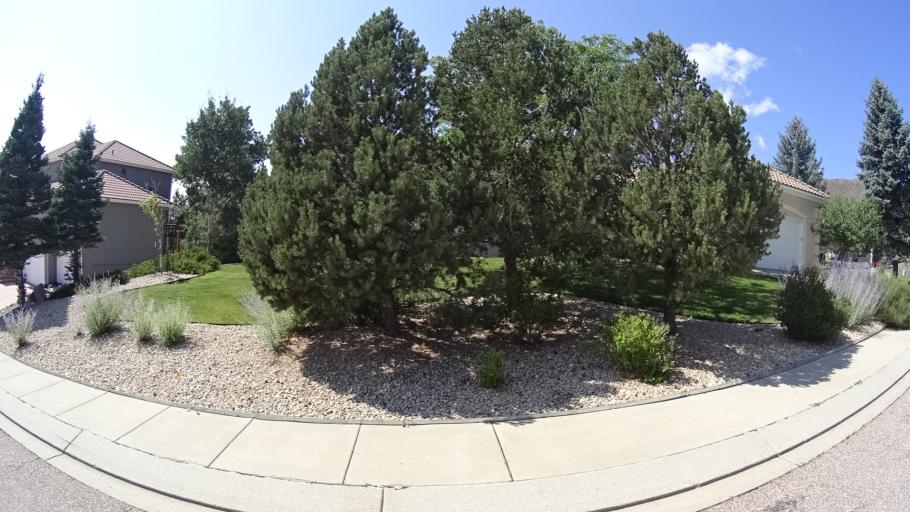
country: US
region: Colorado
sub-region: El Paso County
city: Manitou Springs
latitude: 38.9209
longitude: -104.8801
